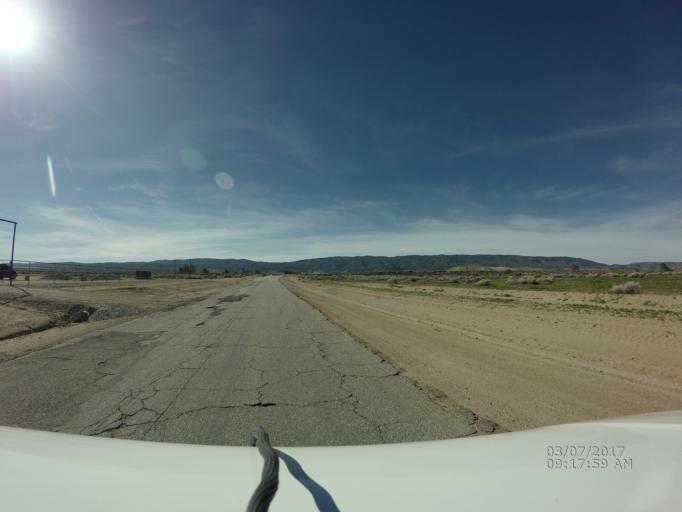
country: US
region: California
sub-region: Los Angeles County
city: Green Valley
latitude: 34.7897
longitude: -118.5901
